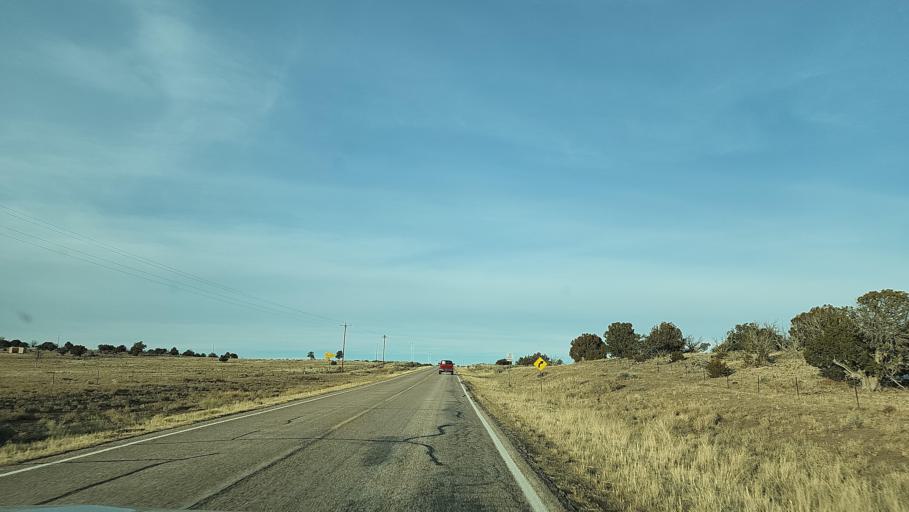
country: US
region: New Mexico
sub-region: Catron County
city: Reserve
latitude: 34.3803
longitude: -108.4583
